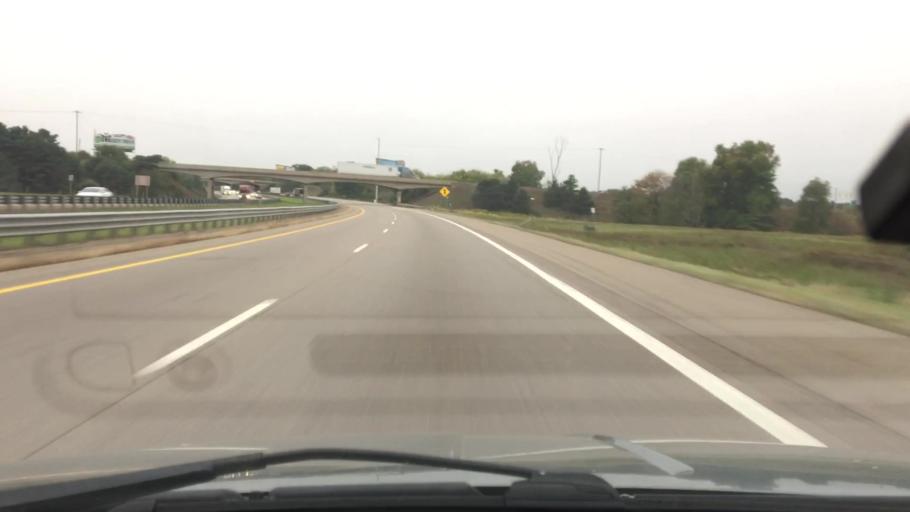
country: US
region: Michigan
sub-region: Calhoun County
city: Brownlee Park
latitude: 42.3001
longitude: -85.0785
